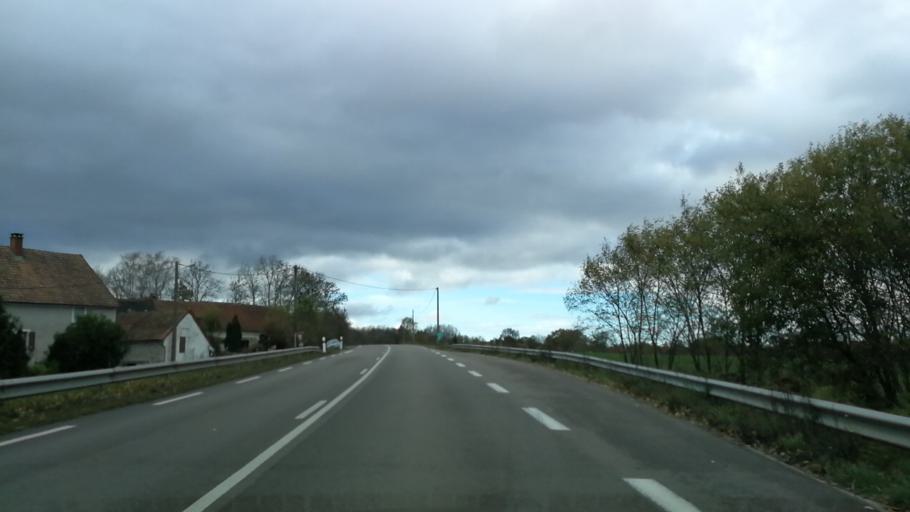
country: FR
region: Bourgogne
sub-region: Departement de la Cote-d'Or
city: Saulieu
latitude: 47.2708
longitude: 4.2525
